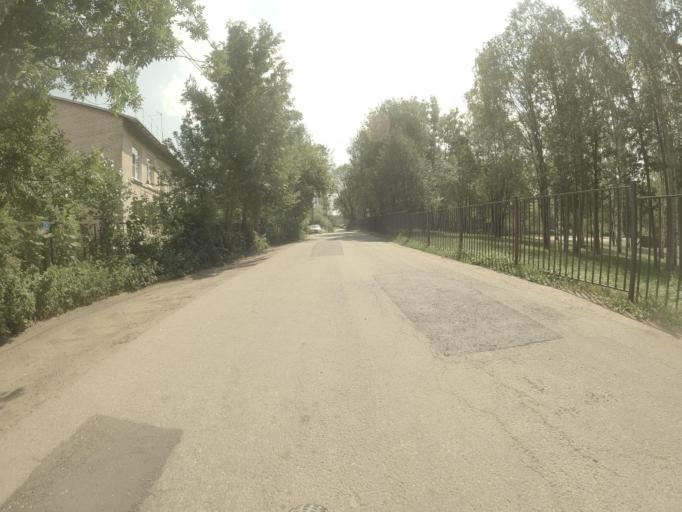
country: RU
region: St.-Petersburg
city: Krasnogvargeisky
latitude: 59.9639
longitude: 30.4720
